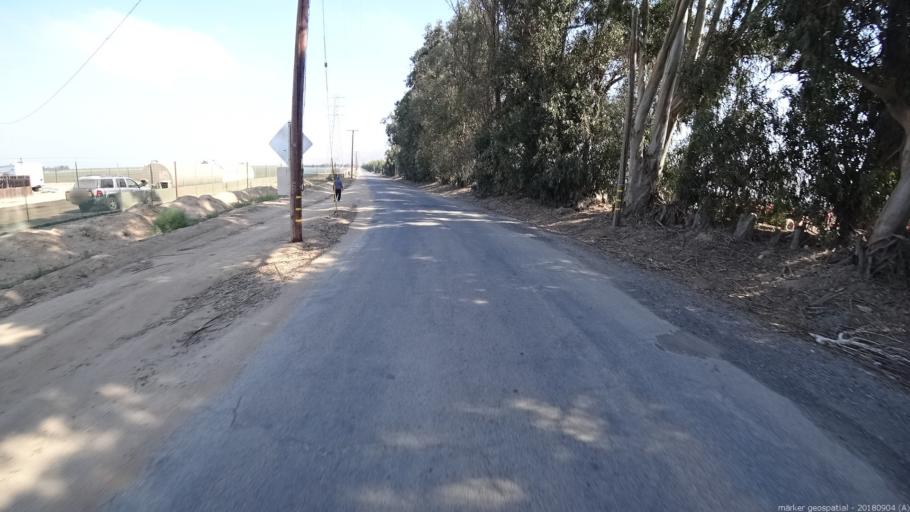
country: US
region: California
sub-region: Monterey County
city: Soledad
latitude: 36.4461
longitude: -121.3318
